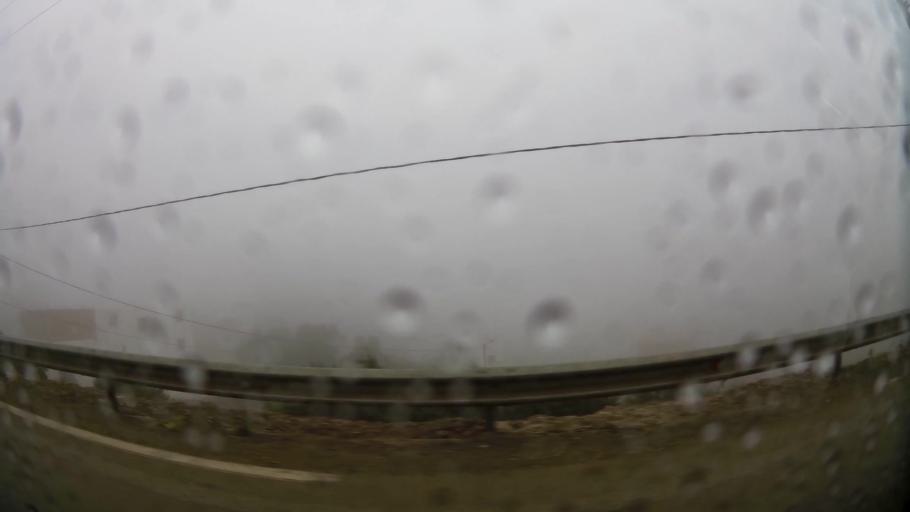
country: MA
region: Taza-Al Hoceima-Taounate
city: Tirhanimine
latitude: 35.2310
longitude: -3.9700
